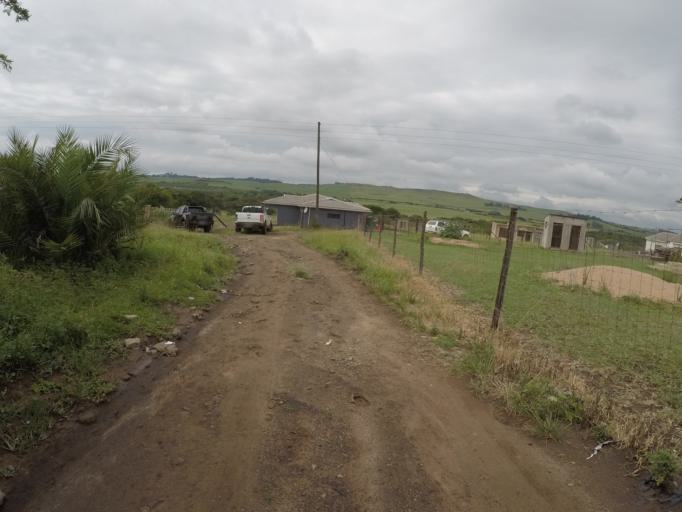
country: ZA
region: KwaZulu-Natal
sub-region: uThungulu District Municipality
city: Empangeni
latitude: -28.7127
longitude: 31.8537
